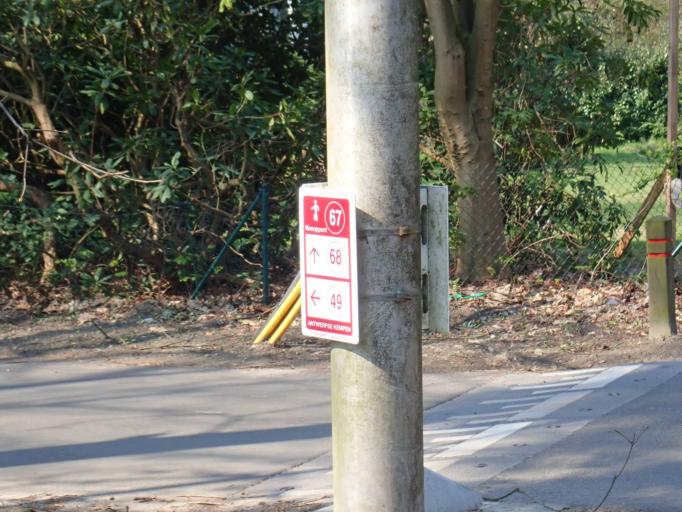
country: BE
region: Flanders
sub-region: Provincie Antwerpen
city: Kalmthout
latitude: 51.3478
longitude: 4.4613
